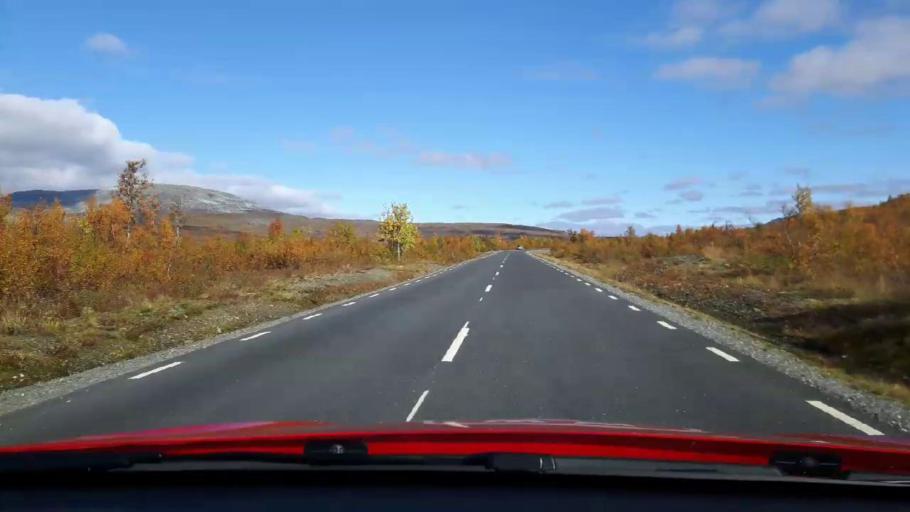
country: NO
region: Nordland
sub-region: Hattfjelldal
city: Hattfjelldal
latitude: 64.9981
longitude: 14.2403
